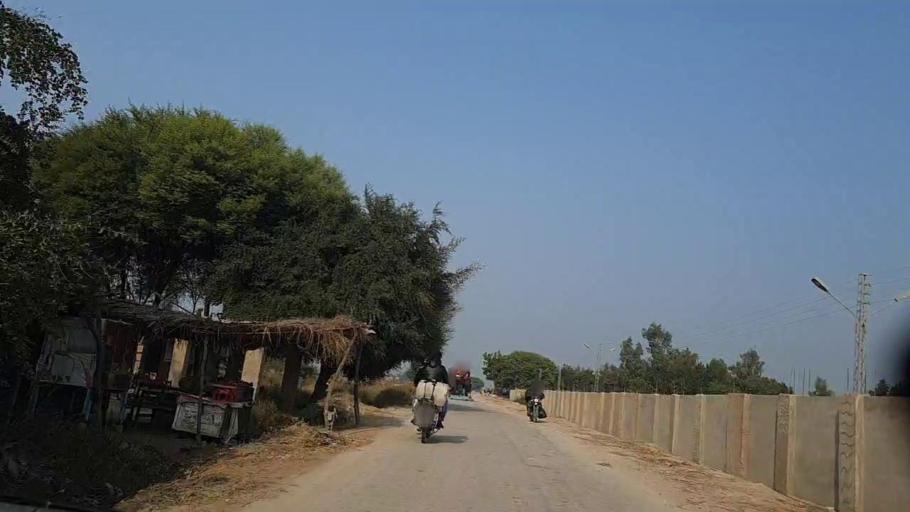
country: PK
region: Sindh
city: Sann
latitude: 26.1810
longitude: 68.1092
